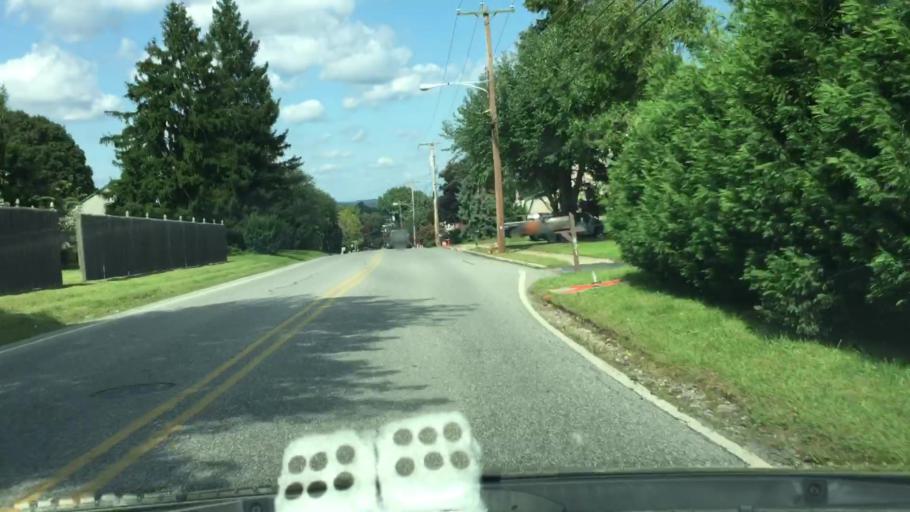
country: US
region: Pennsylvania
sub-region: Montgomery County
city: Norristown
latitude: 40.1213
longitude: -75.3070
